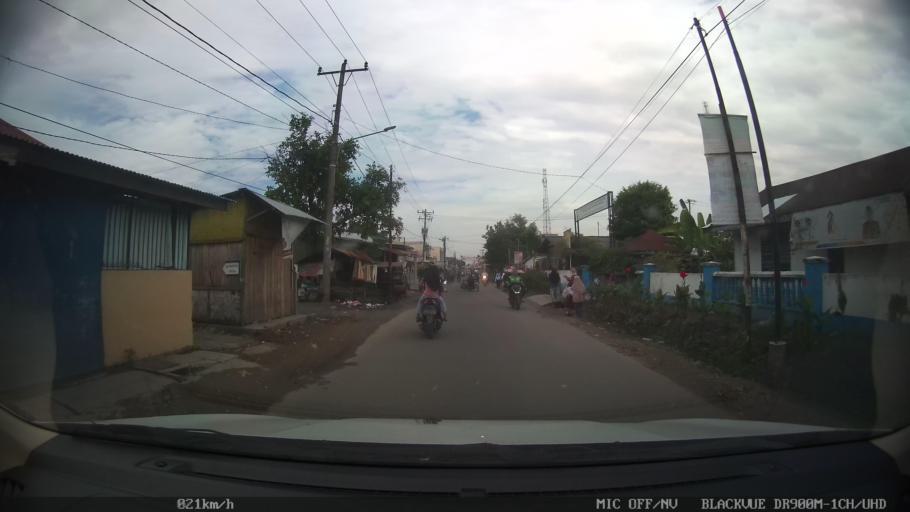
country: ID
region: North Sumatra
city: Sunggal
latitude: 3.6403
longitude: 98.5941
